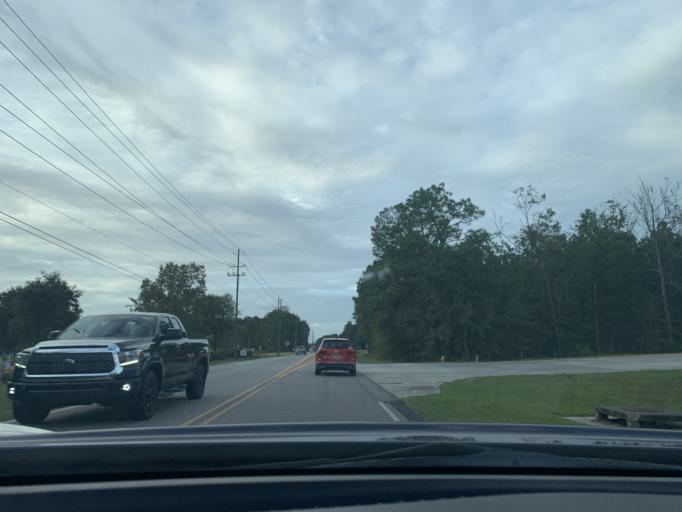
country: US
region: Georgia
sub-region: Chatham County
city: Pooler
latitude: 32.0652
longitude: -81.2732
